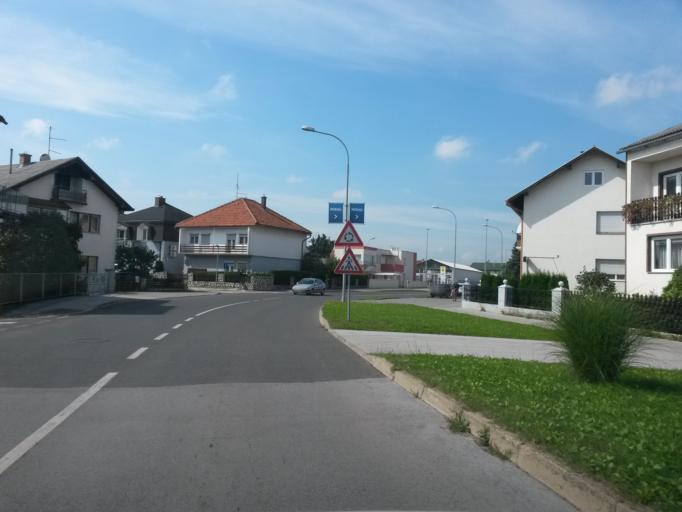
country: HR
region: Varazdinska
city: Varazdin
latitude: 46.2966
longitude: 16.3293
